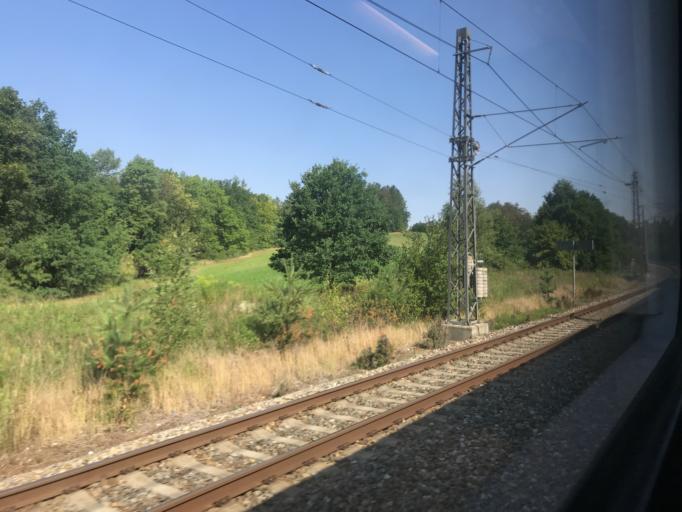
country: CZ
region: Central Bohemia
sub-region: Okres Praha-Vychod
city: Mnichovice
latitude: 49.9017
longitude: 14.7277
